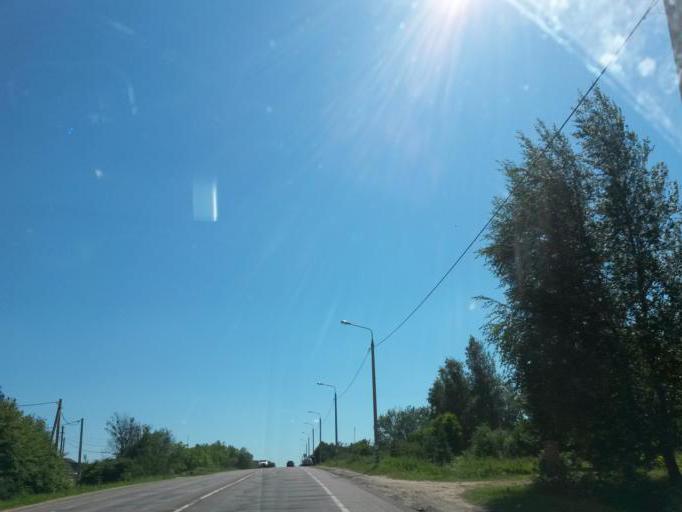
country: RU
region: Moskovskaya
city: Proletarskiy
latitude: 55.0676
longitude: 37.4367
